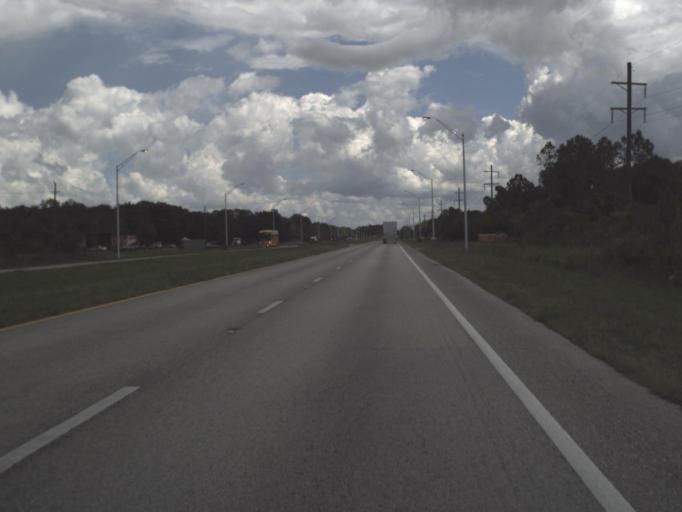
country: US
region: Florida
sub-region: Polk County
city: Babson Park
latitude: 27.8760
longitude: -81.4056
